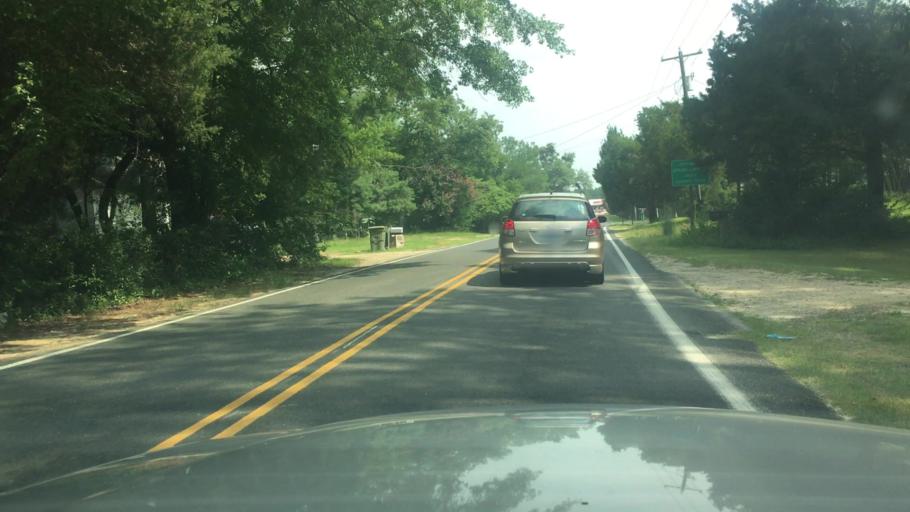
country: US
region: North Carolina
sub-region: Cumberland County
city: Hope Mills
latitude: 35.0028
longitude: -78.9649
